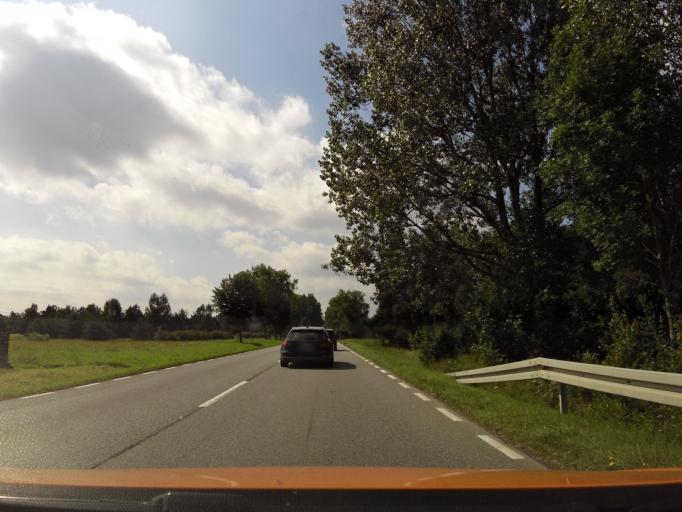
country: PL
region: West Pomeranian Voivodeship
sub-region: Powiat gryficki
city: Ploty
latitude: 53.8165
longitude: 15.2795
